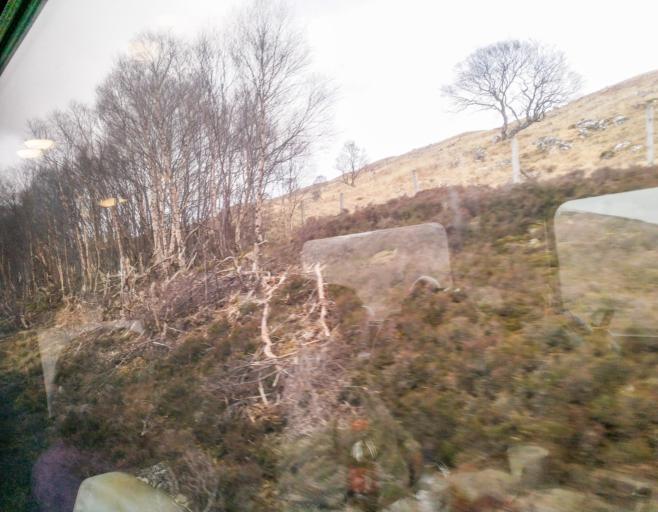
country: GB
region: Scotland
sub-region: Highland
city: Spean Bridge
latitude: 56.7825
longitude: -4.7328
